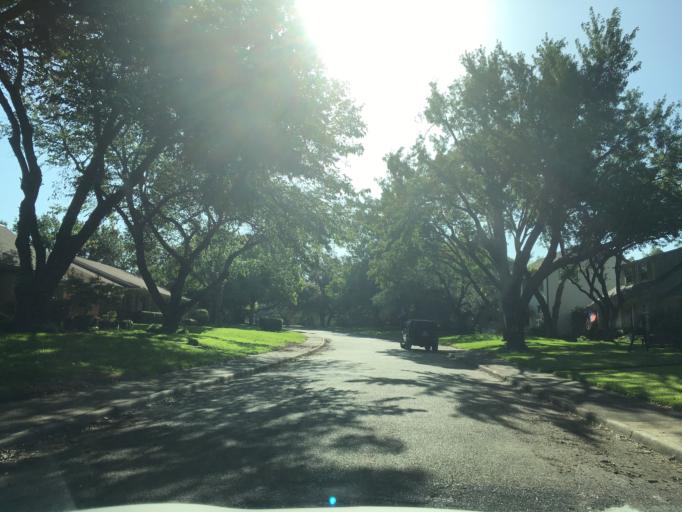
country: US
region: Texas
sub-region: Dallas County
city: Richardson
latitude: 32.8811
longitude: -96.7260
